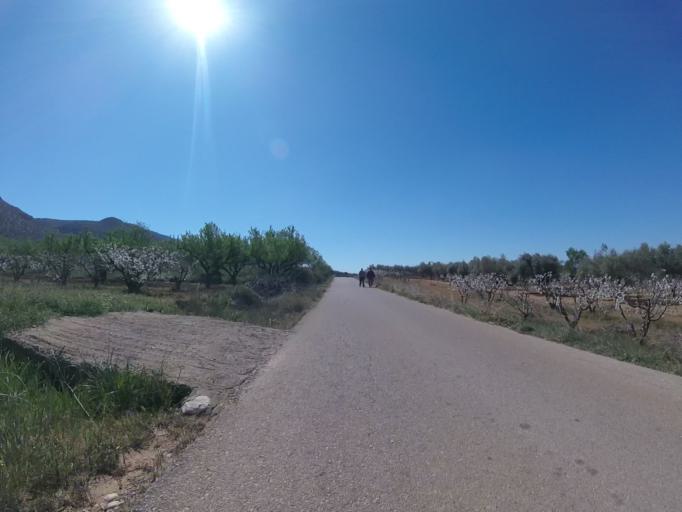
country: ES
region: Valencia
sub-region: Provincia de Castello
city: Cervera del Maestre
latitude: 40.4087
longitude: 0.1750
